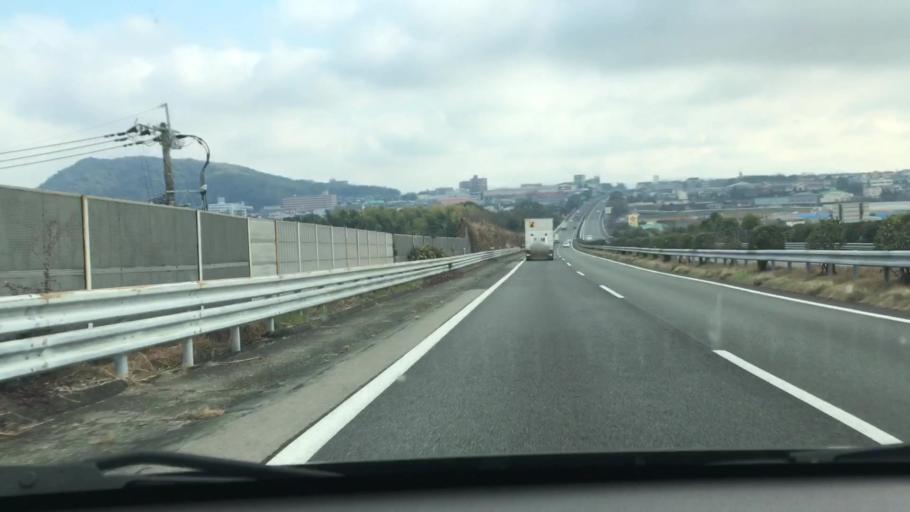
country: JP
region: Kumamoto
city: Kumamoto
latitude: 32.8467
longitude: 130.7696
